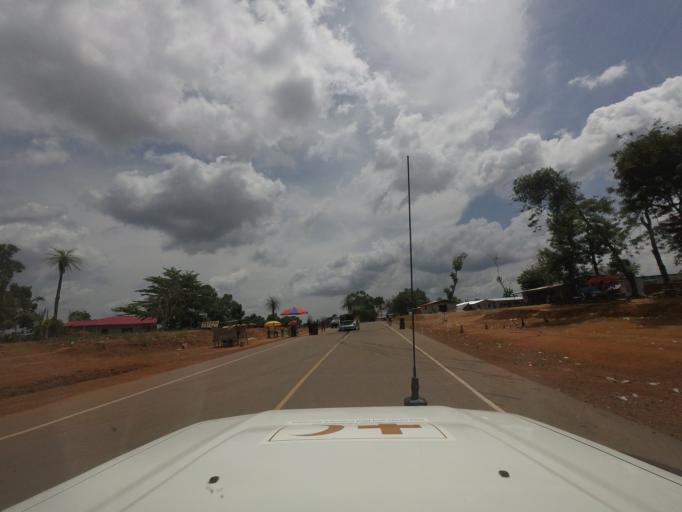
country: LR
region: Nimba
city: Sanniquellie
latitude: 7.2492
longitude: -8.9829
